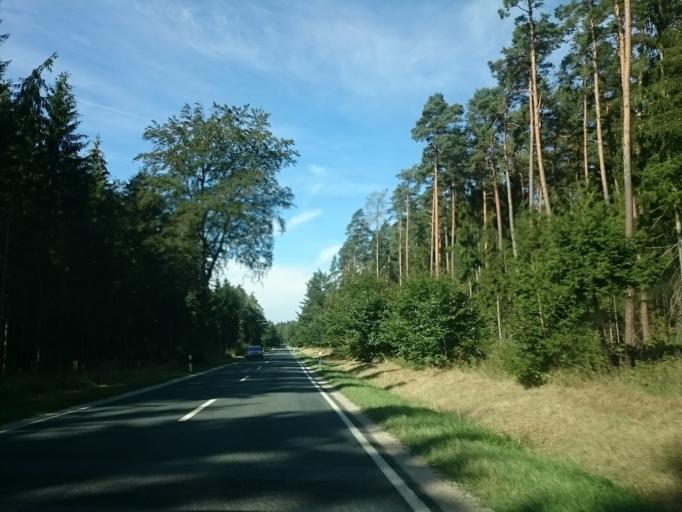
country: DE
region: Bavaria
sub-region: Regierungsbezirk Mittelfranken
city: Rottenbach
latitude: 49.1333
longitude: 11.0607
